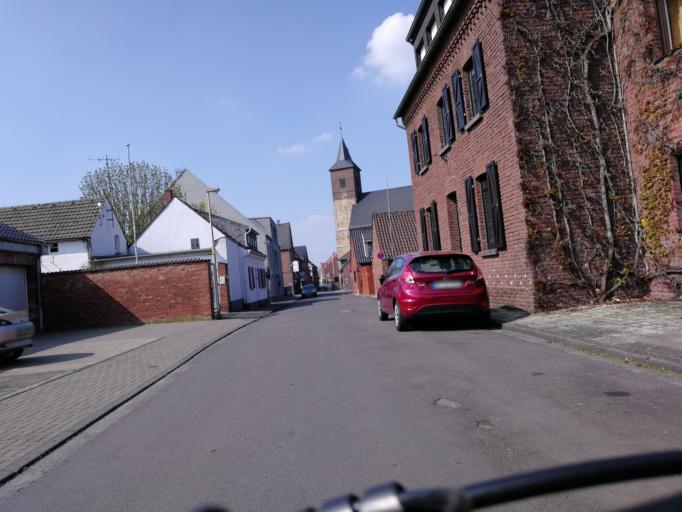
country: DE
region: North Rhine-Westphalia
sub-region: Regierungsbezirk Dusseldorf
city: Dormagen
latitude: 51.1127
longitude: 6.7733
